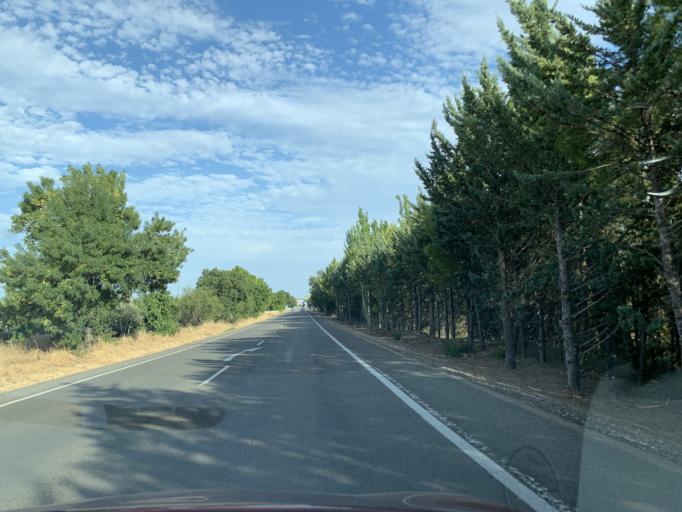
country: ES
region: Aragon
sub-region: Provincia de Huesca
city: Chimillas
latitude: 42.1525
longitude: -0.4351
